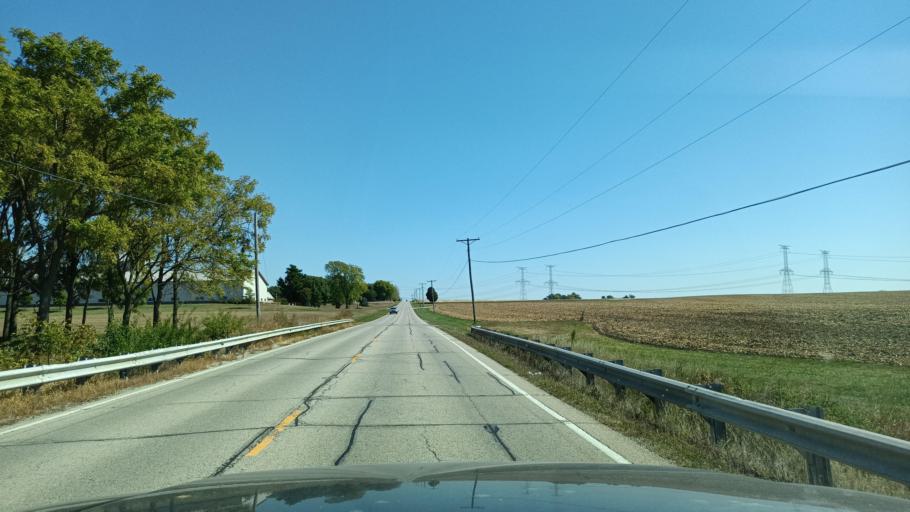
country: US
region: Illinois
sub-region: Tazewell County
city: Morton
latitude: 40.6136
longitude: -89.4181
